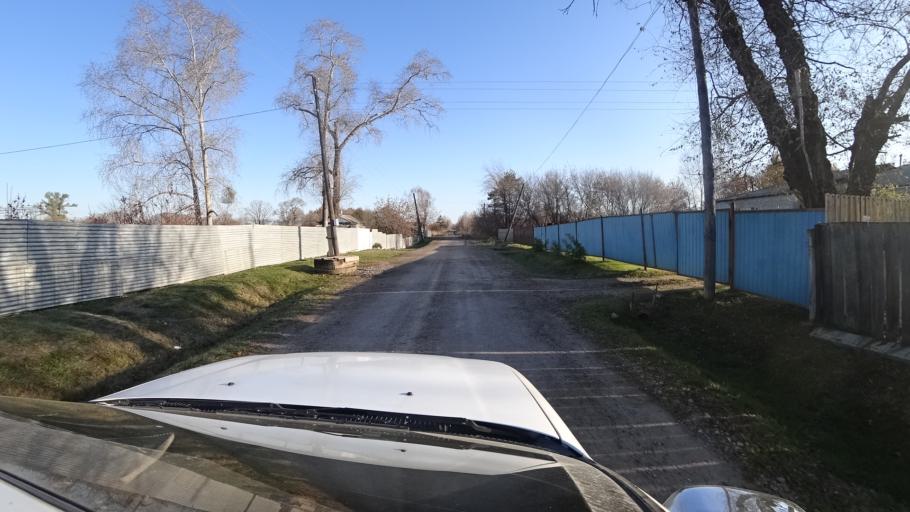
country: RU
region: Primorskiy
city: Lazo
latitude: 45.8726
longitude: 133.6451
